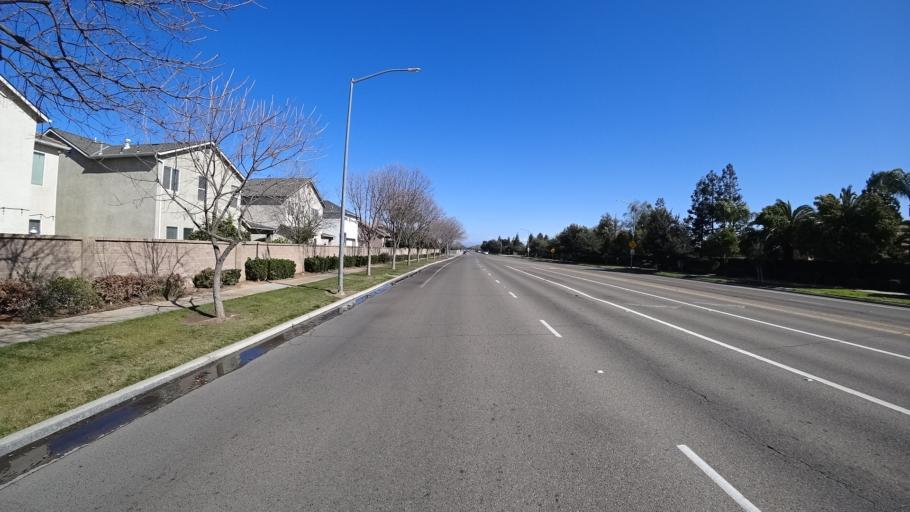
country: US
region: California
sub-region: Fresno County
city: Clovis
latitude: 36.8596
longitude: -119.7292
